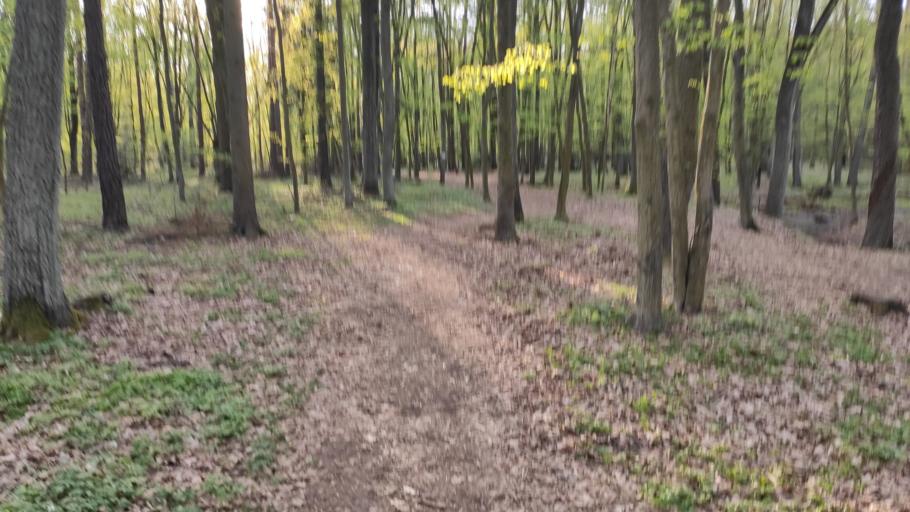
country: PL
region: Masovian Voivodeship
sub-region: Powiat radomski
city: Pionki
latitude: 51.4749
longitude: 21.4365
